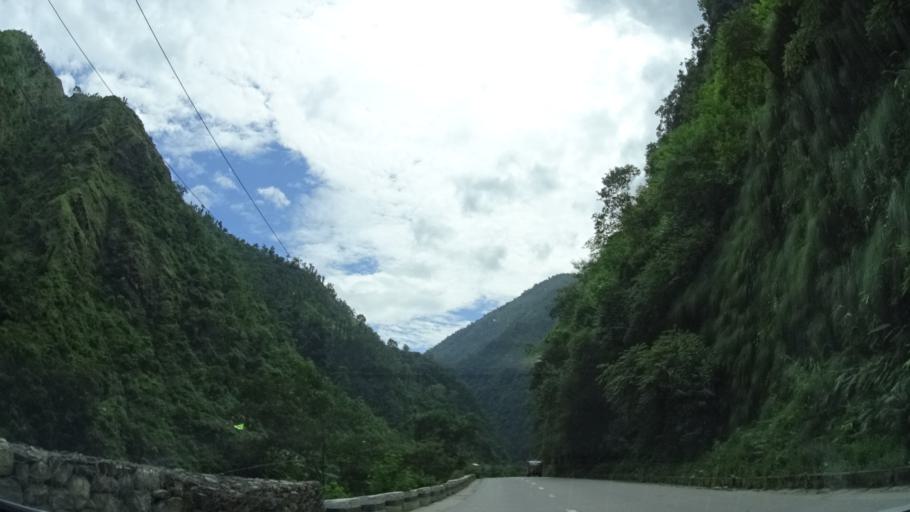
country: NP
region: Central Region
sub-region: Narayani Zone
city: Bharatpur
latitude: 27.8233
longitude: 84.6662
